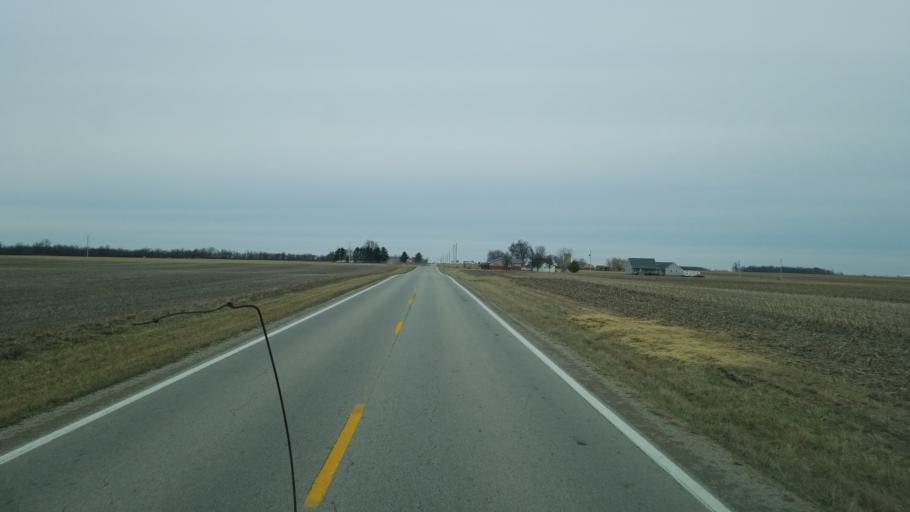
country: US
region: Ohio
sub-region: Ross County
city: Frankfort
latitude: 39.4530
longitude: -83.2123
